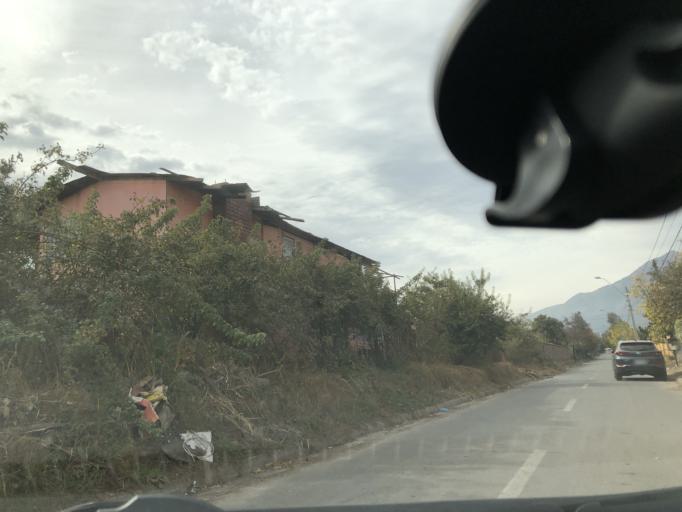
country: CL
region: Santiago Metropolitan
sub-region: Provincia de Cordillera
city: Puente Alto
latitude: -33.6122
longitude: -70.5354
